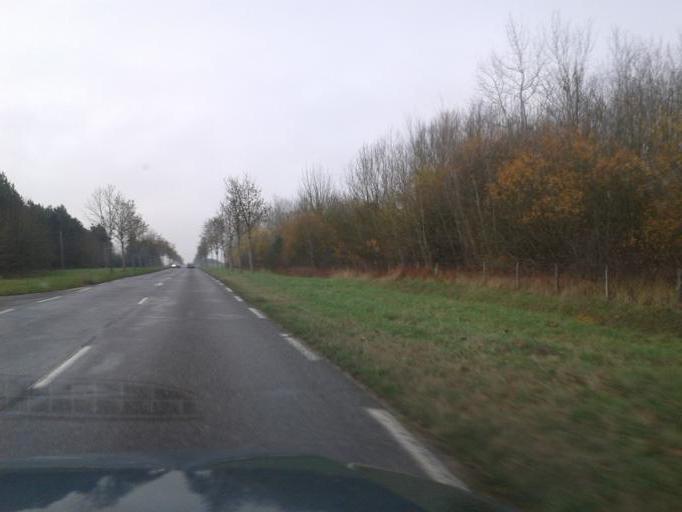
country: FR
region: Centre
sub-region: Departement du Loiret
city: Dry
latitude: 47.8006
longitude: 1.7301
